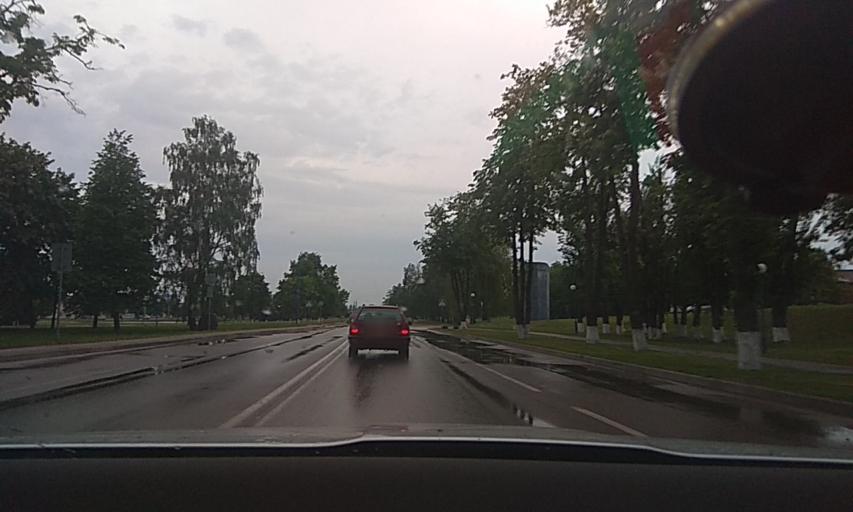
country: BY
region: Grodnenskaya
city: Hrodna
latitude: 53.6763
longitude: 23.8892
